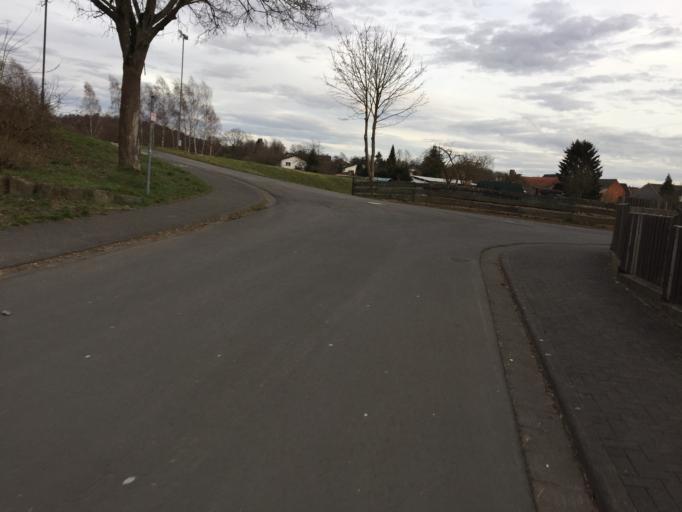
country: DE
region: Hesse
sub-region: Regierungsbezirk Giessen
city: Rabenau
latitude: 50.6719
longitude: 8.8721
